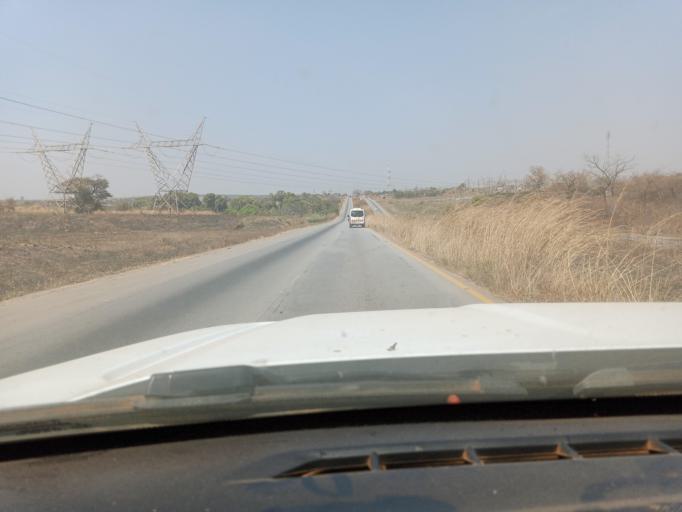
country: ZM
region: Copperbelt
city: Luanshya
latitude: -12.9683
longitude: 28.3977
